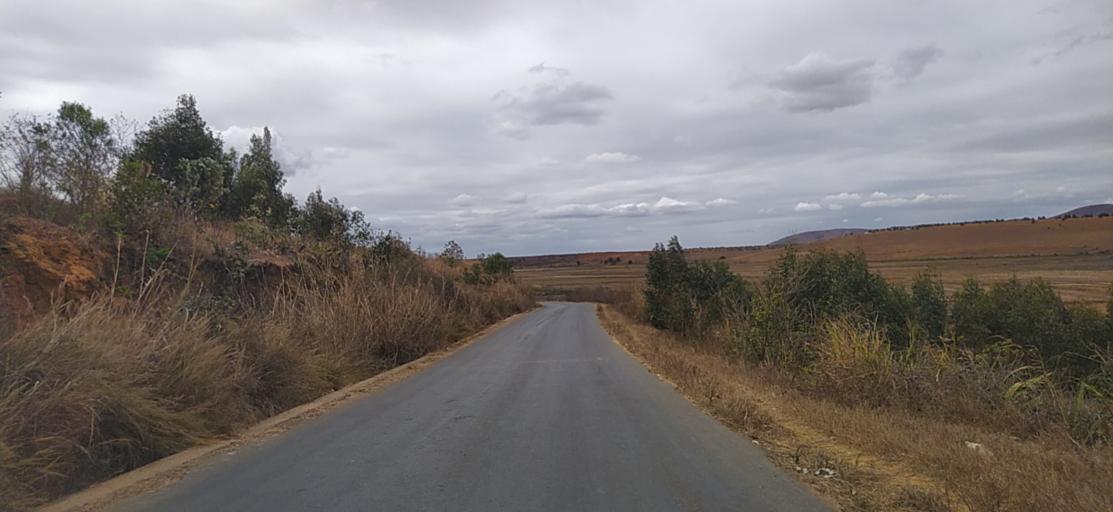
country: MG
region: Alaotra Mangoro
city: Ambatondrazaka
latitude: -17.9267
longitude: 48.2578
